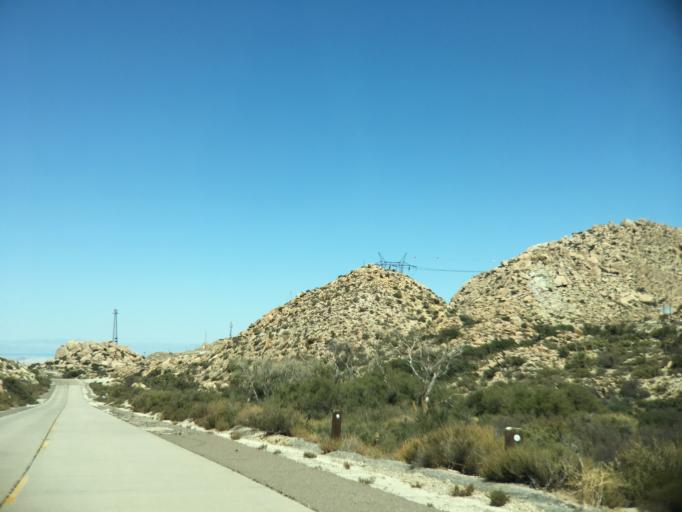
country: MX
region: Baja California
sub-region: Tecate
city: Cereso del Hongo
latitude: 32.6508
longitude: -116.1032
